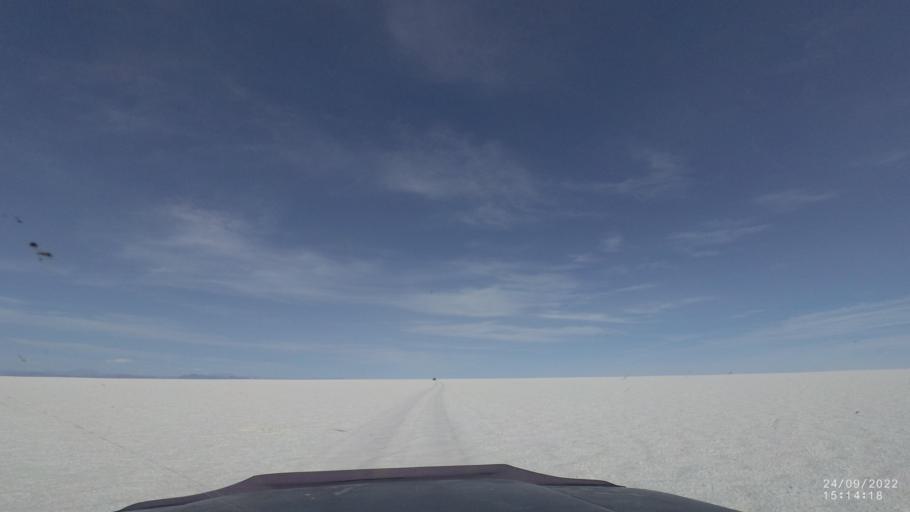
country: BO
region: Potosi
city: Colchani
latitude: -19.9629
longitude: -67.4566
